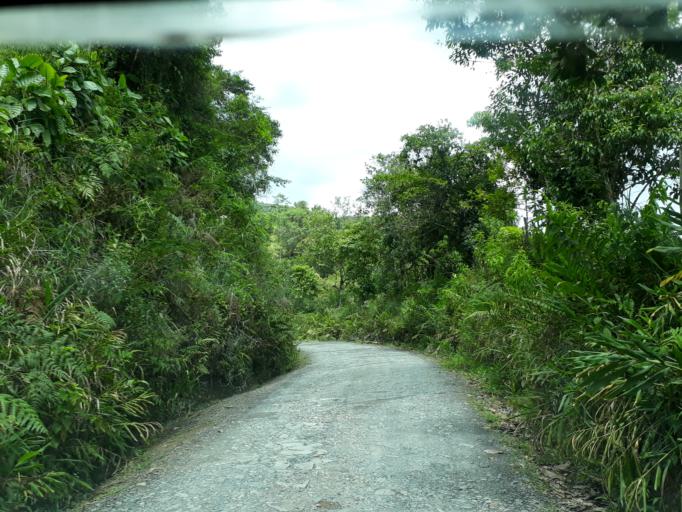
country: CO
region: Cundinamarca
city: Topaipi
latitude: 5.3479
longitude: -74.1922
